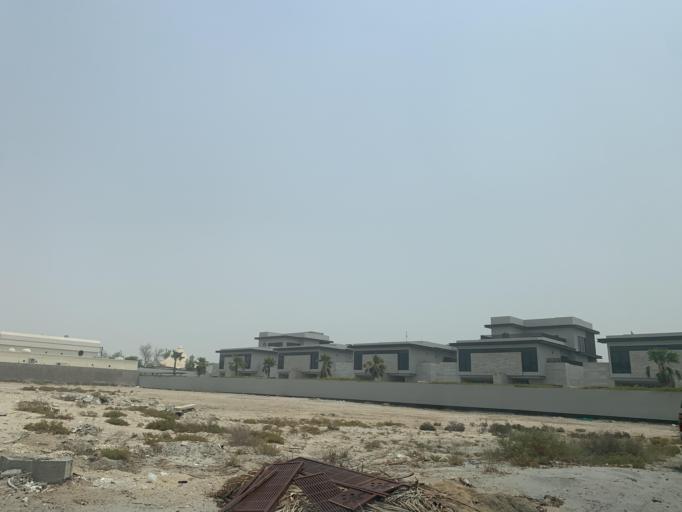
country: BH
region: Central Governorate
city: Madinat Hamad
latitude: 26.1700
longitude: 50.4723
